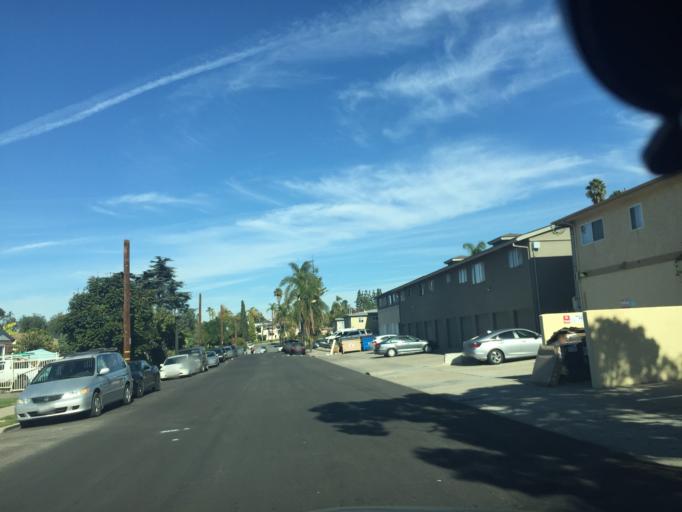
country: US
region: California
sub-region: San Diego County
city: Lemon Grove
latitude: 32.7575
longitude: -117.0929
